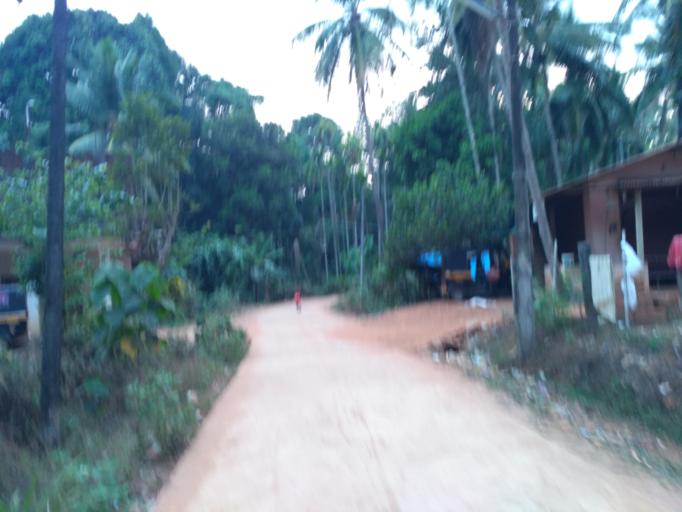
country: IN
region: Karnataka
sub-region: Kodagu
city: Somvarpet
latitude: 12.6609
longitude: 75.6167
